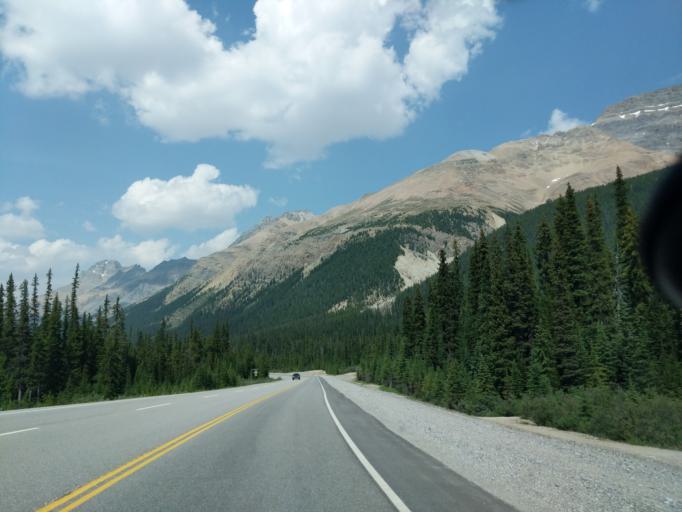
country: CA
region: Alberta
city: Lake Louise
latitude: 51.7263
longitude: -116.5011
